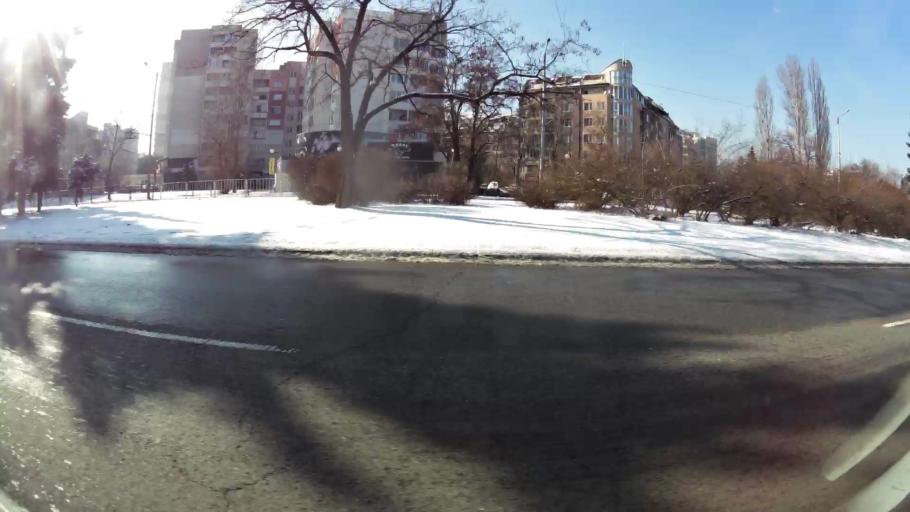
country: BG
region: Sofia-Capital
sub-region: Stolichna Obshtina
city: Sofia
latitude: 42.6780
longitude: 23.3031
